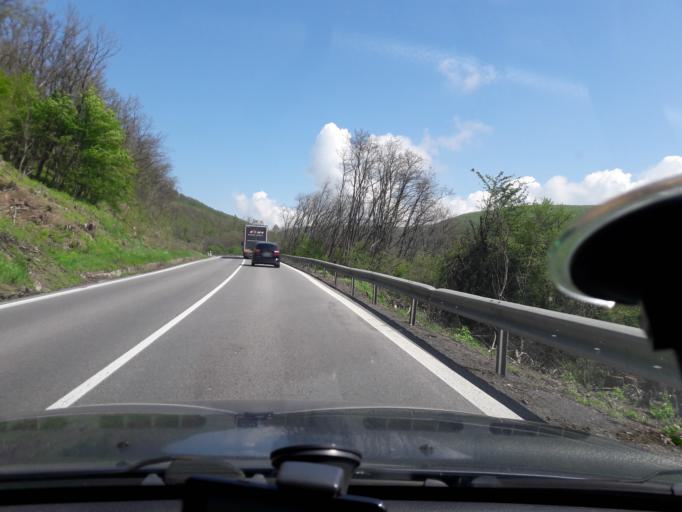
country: SK
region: Banskobystricky
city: Krupina
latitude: 48.3793
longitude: 19.0767
